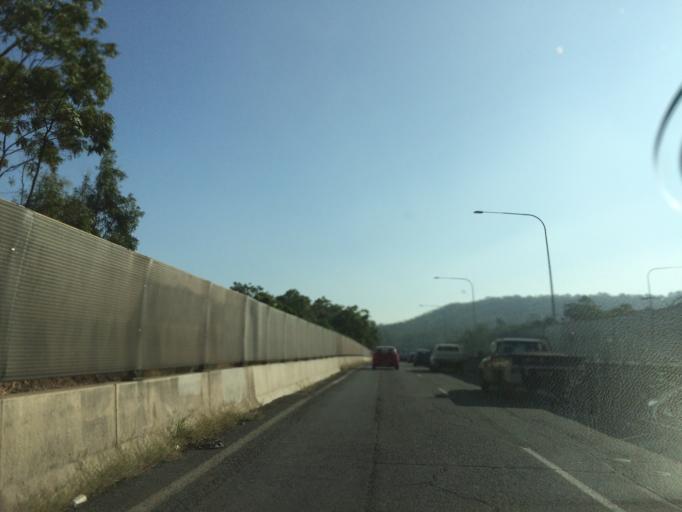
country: AU
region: Queensland
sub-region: Brisbane
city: Taringa
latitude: -27.4796
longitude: 152.9761
